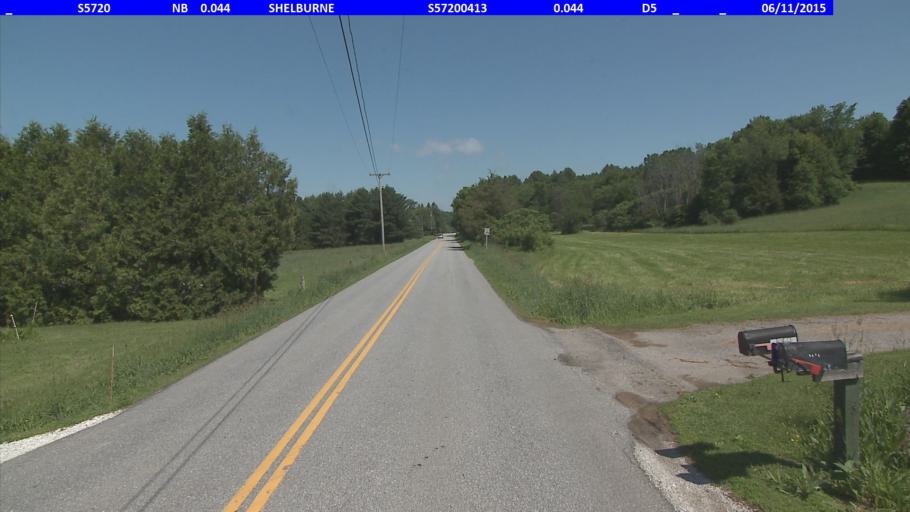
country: US
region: Vermont
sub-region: Chittenden County
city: Hinesburg
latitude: 44.3591
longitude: -73.1966
